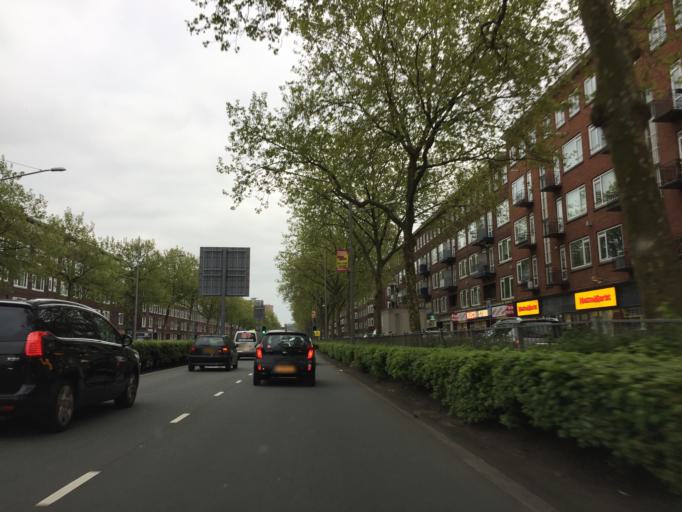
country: NL
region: South Holland
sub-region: Gemeente Rotterdam
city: Delfshaven
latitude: 51.8913
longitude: 4.4804
